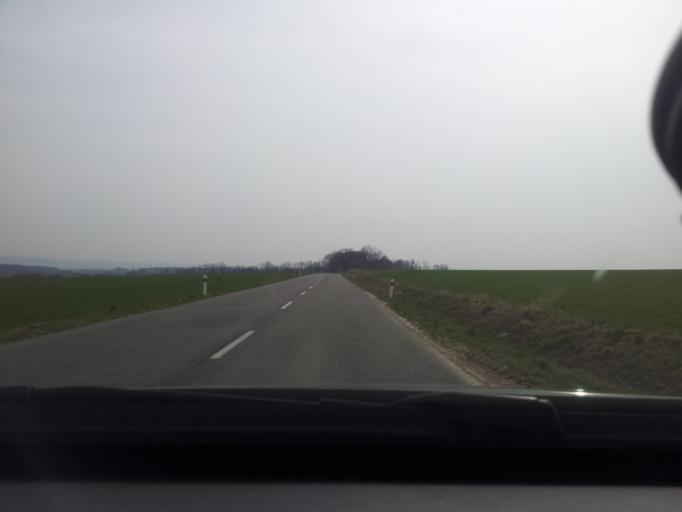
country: SK
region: Trnavsky
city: Leopoldov
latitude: 48.4635
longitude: 17.7035
